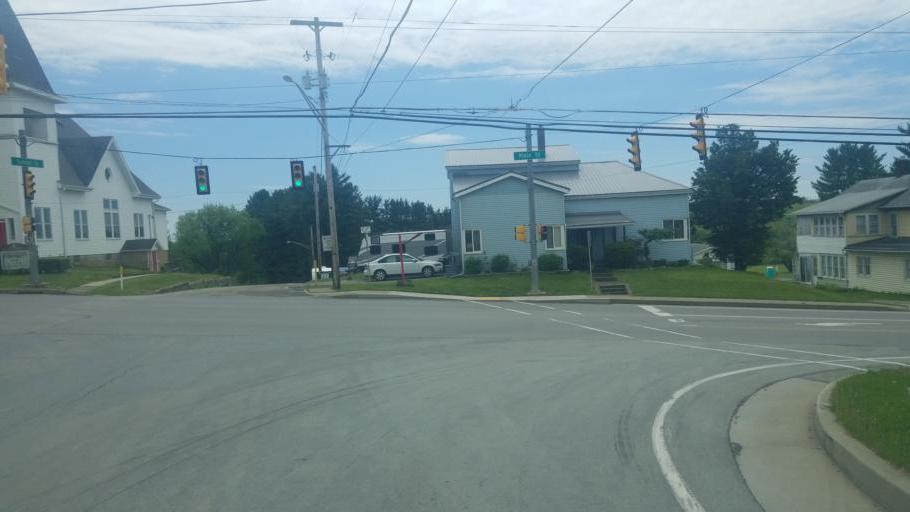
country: US
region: Pennsylvania
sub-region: Clarion County
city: Marianne
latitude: 41.2507
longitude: -79.4596
